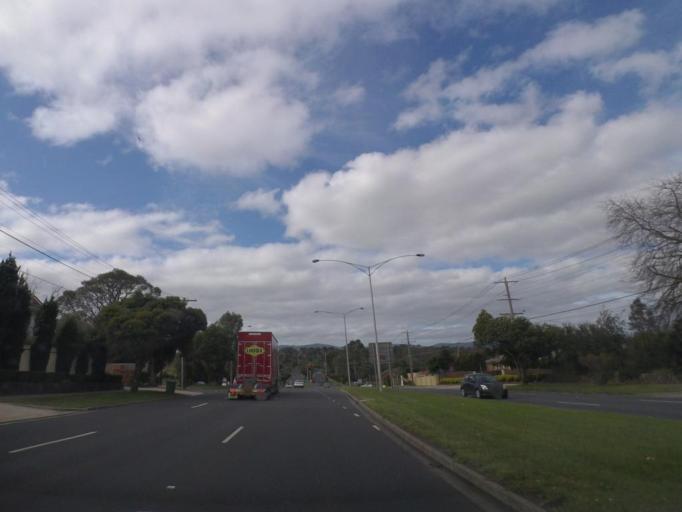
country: AU
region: Victoria
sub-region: Knox
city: Wantirna
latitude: -37.8323
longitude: 145.2255
